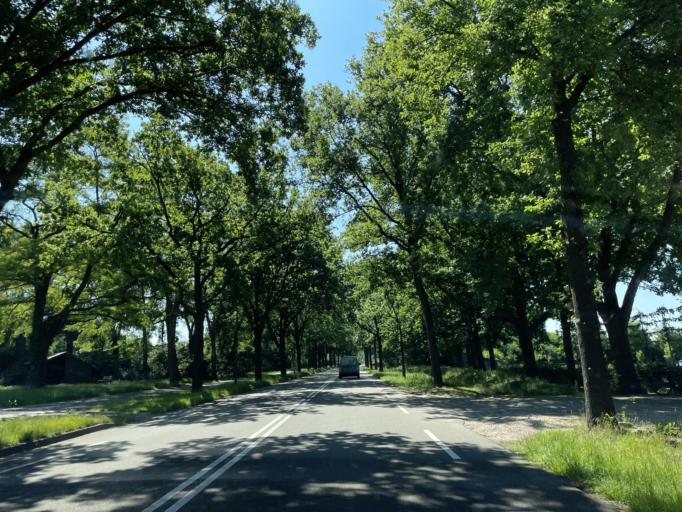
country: NL
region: North Brabant
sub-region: Gemeente 's-Hertogenbosch
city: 's-Hertogenbosch
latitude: 51.7140
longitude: 5.3504
